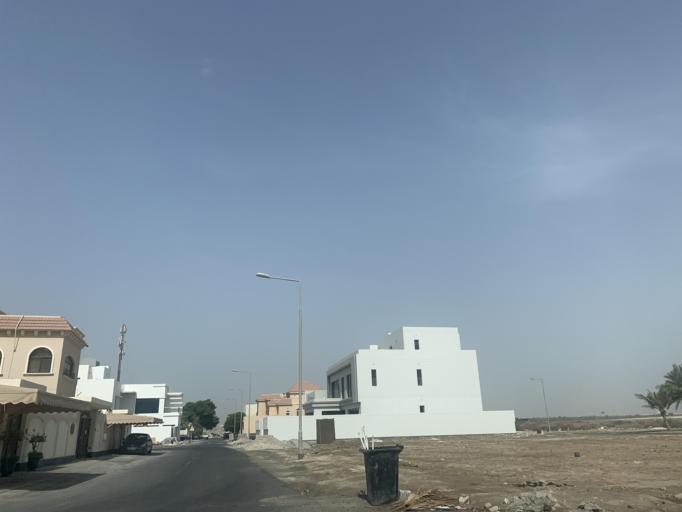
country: BH
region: Northern
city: Madinat `Isa
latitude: 26.1918
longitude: 50.4936
